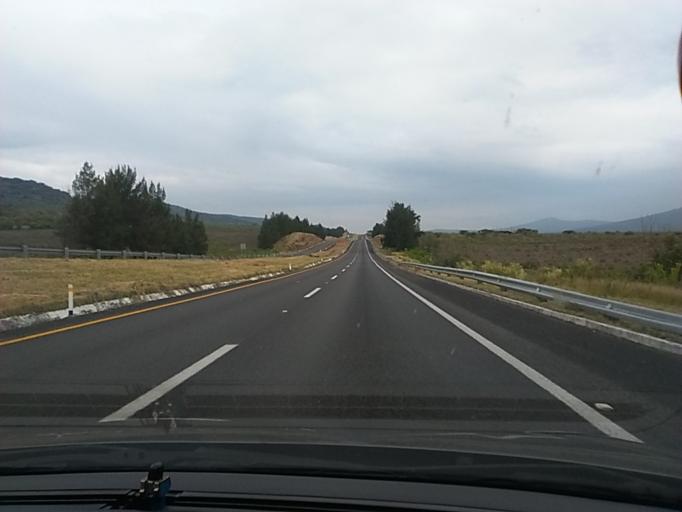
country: MX
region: Michoacan
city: Churintzio
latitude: 20.1193
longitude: -102.0517
